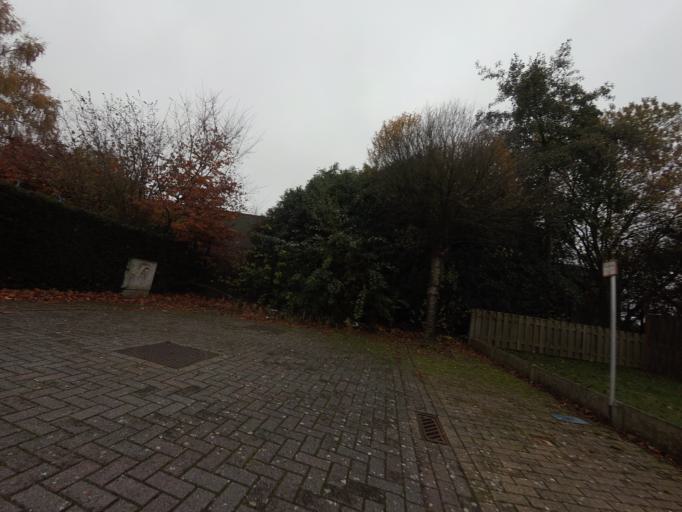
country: BE
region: Flanders
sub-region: Provincie Vlaams-Brabant
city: Zaventem
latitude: 50.8782
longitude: 4.4982
